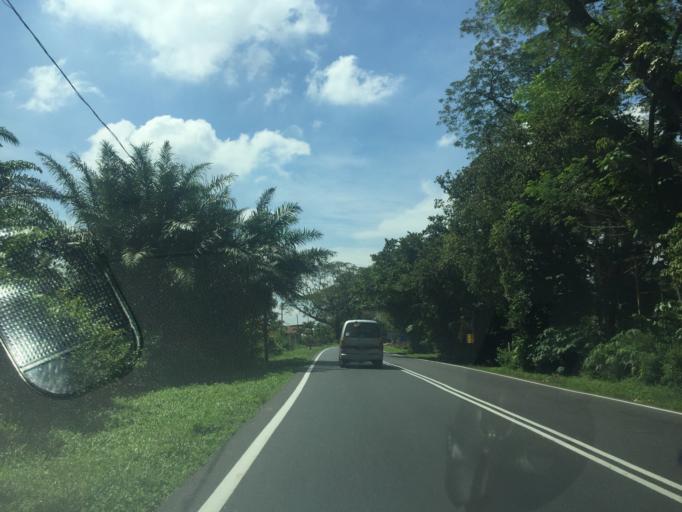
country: MY
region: Penang
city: Tasek Glugor
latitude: 5.5076
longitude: 100.5285
